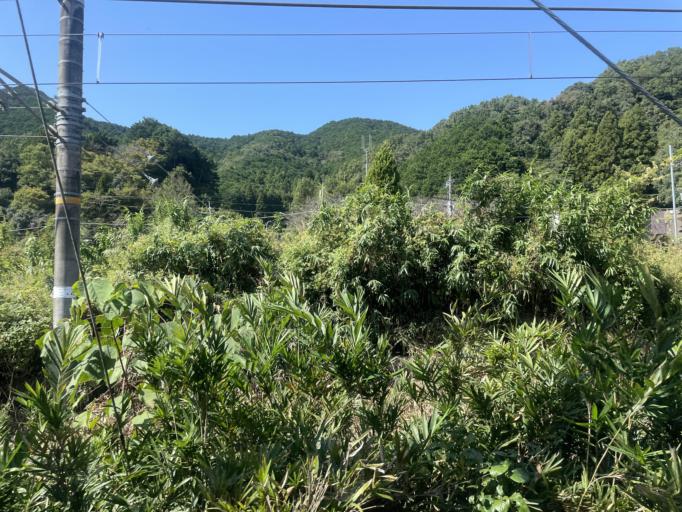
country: JP
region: Nara
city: Gose
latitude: 34.4236
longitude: 135.7513
